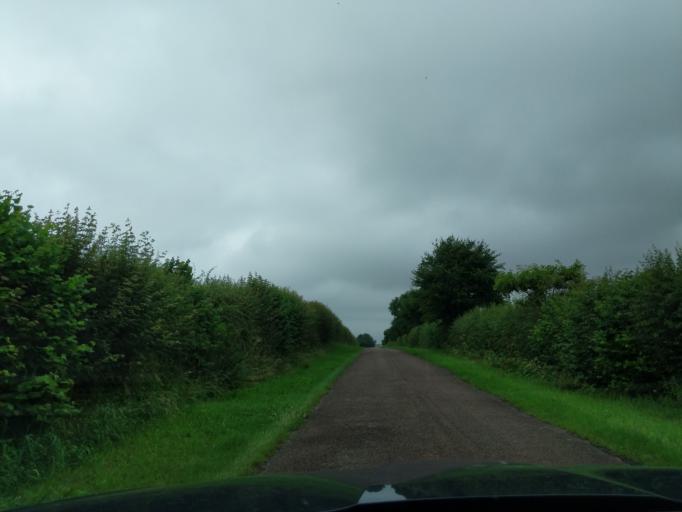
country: GB
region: England
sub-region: Northumberland
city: Ford
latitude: 55.6854
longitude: -2.1259
